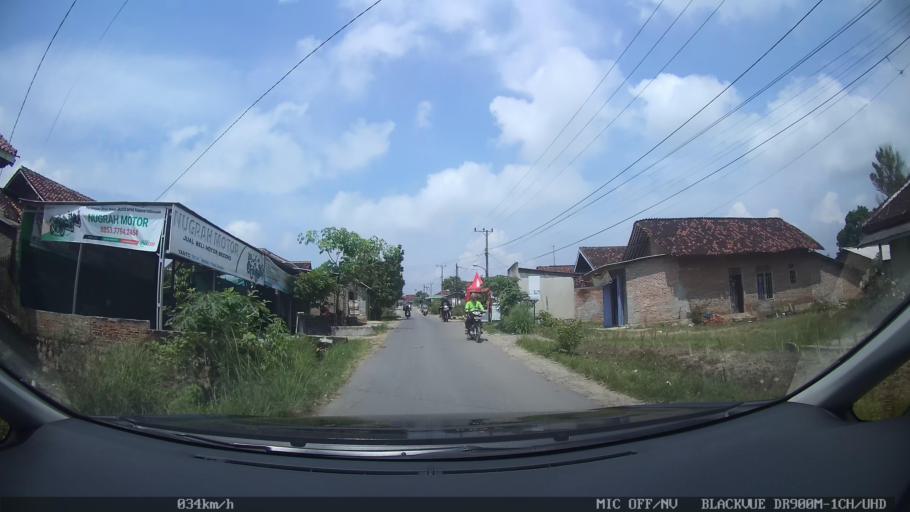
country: ID
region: Lampung
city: Kedaton
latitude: -5.3361
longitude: 105.2991
